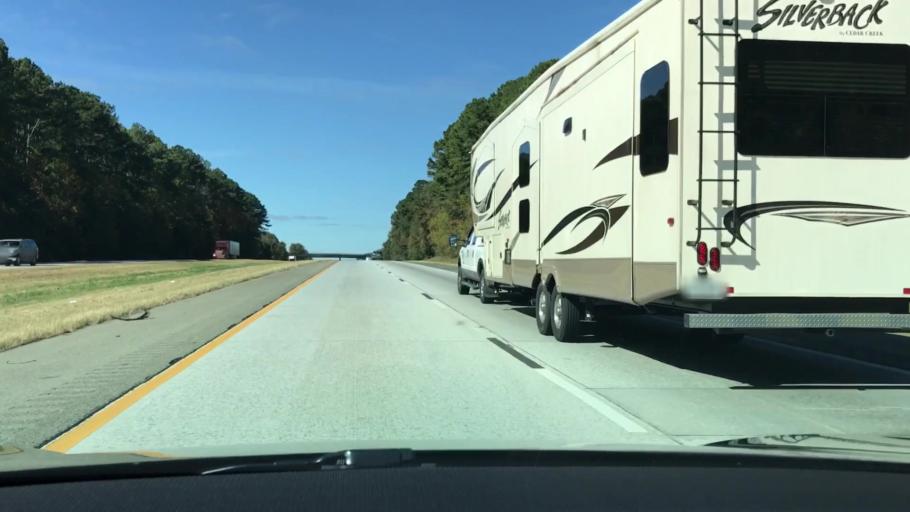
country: US
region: Georgia
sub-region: Putnam County
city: Jefferson
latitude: 33.5379
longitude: -83.3083
